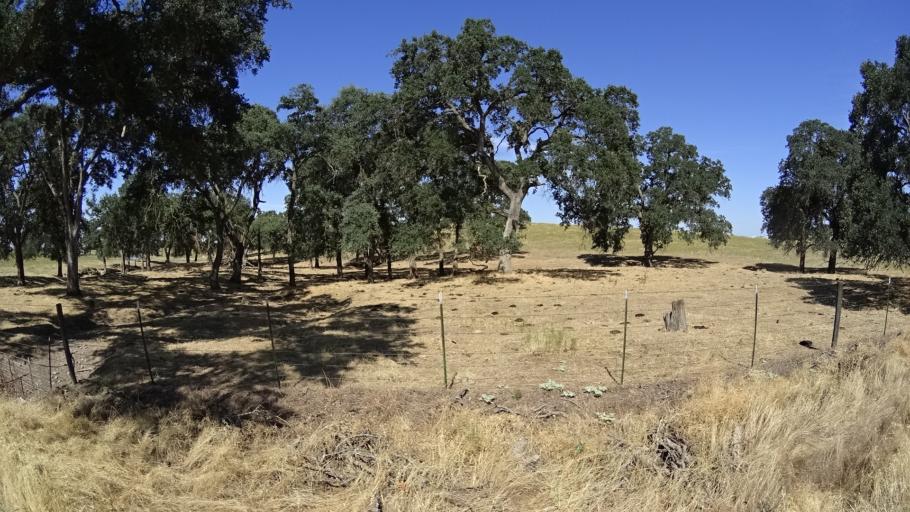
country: US
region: California
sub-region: Calaveras County
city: Rancho Calaveras
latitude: 38.0885
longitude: -120.9264
